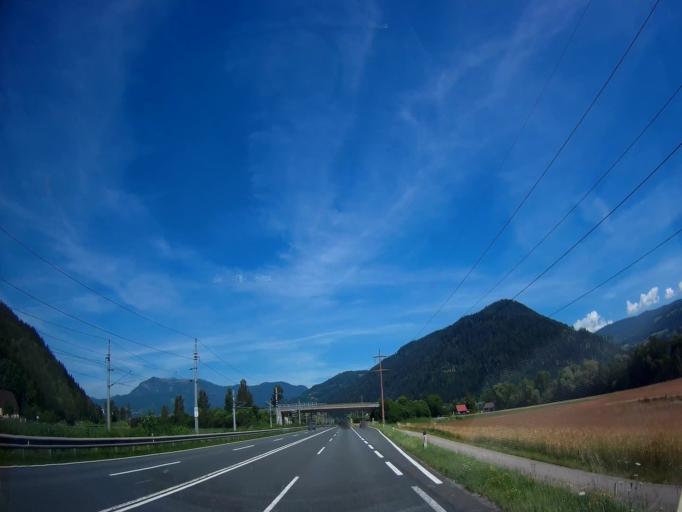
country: AT
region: Carinthia
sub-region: Politischer Bezirk Sankt Veit an der Glan
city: Micheldorf
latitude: 46.9377
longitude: 14.4252
